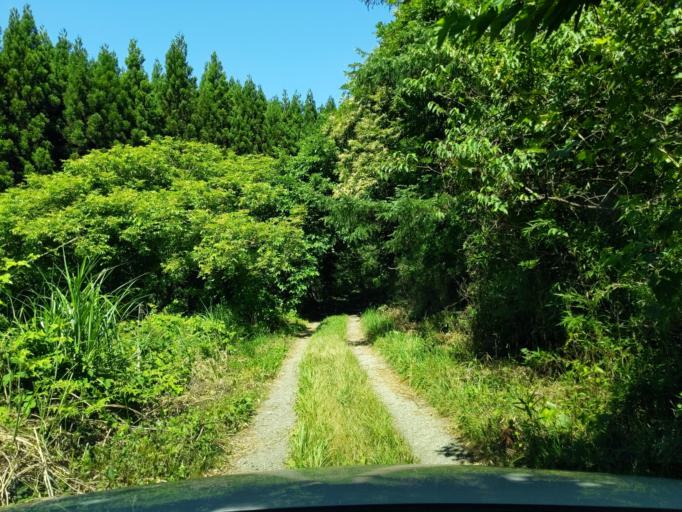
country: JP
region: Fukushima
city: Koriyama
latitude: 37.3880
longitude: 140.2488
